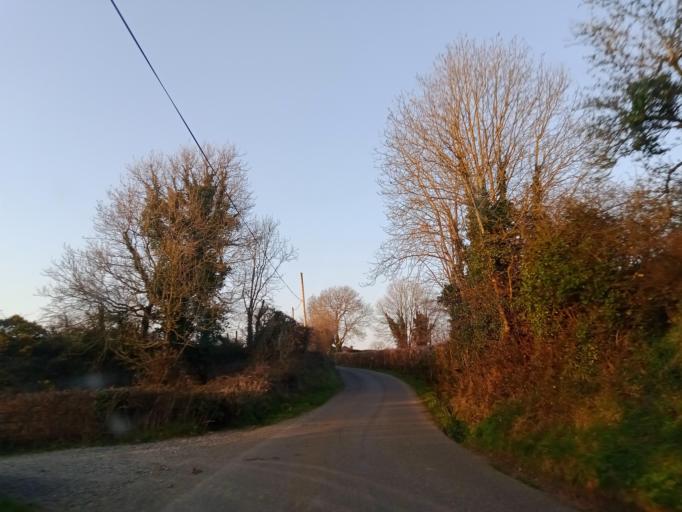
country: IE
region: Leinster
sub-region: Kilkenny
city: Kilkenny
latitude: 52.7257
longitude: -7.2372
